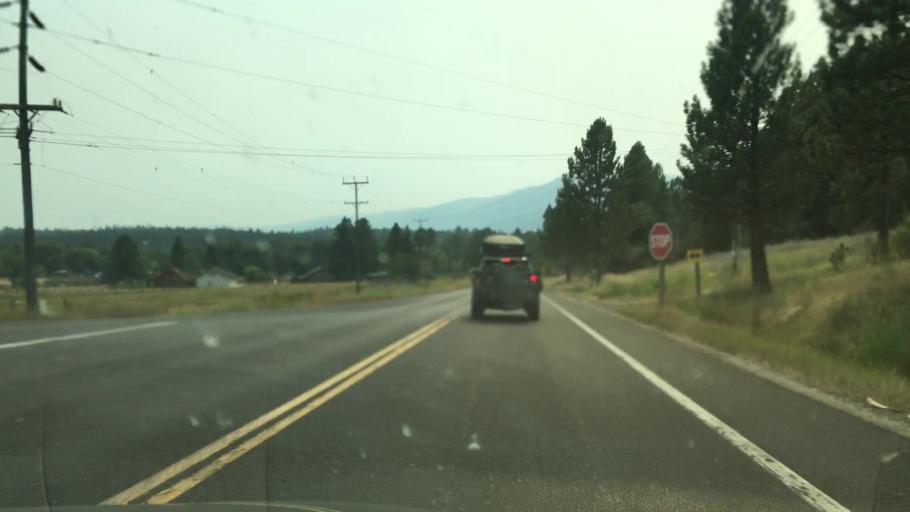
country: US
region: Idaho
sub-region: Valley County
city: Cascade
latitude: 44.5280
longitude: -116.0412
